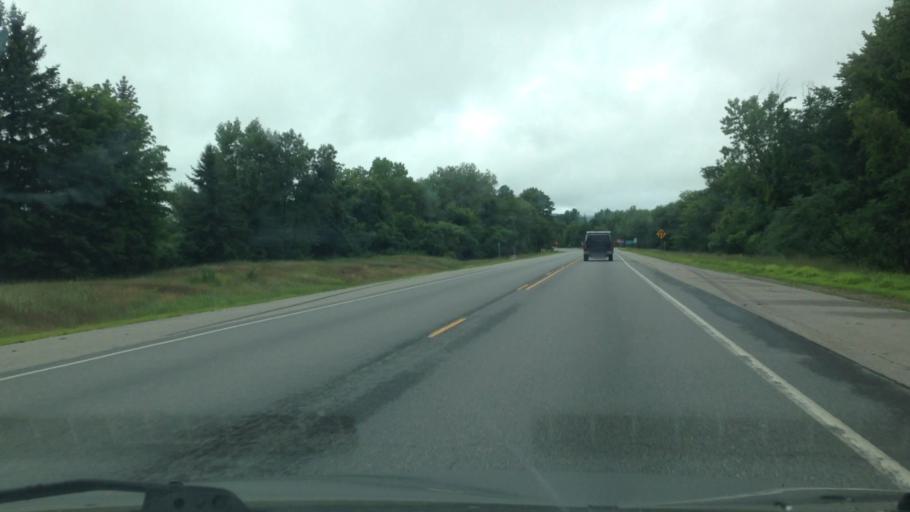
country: US
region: New Hampshire
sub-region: Cheshire County
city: Keene
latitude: 42.9183
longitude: -72.2685
